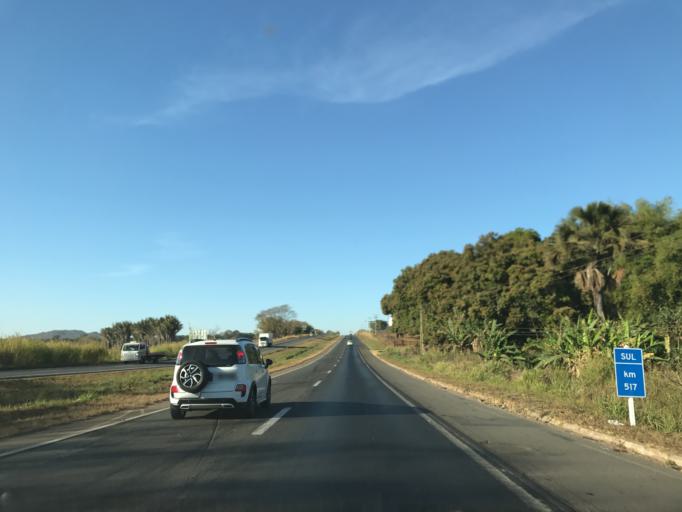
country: BR
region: Goias
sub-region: Aparecida De Goiania
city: Aparecida de Goiania
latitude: -16.8501
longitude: -49.2472
